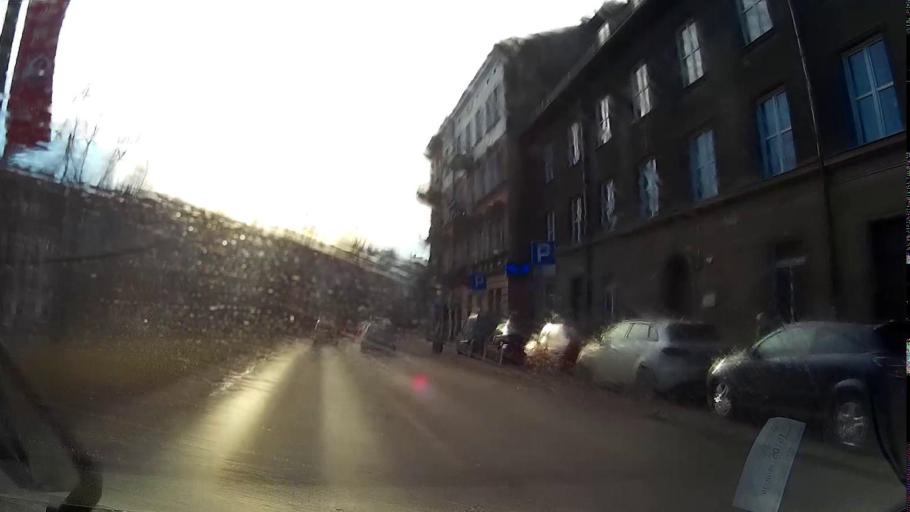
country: PL
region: Lesser Poland Voivodeship
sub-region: Krakow
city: Krakow
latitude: 50.0514
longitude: 19.9409
